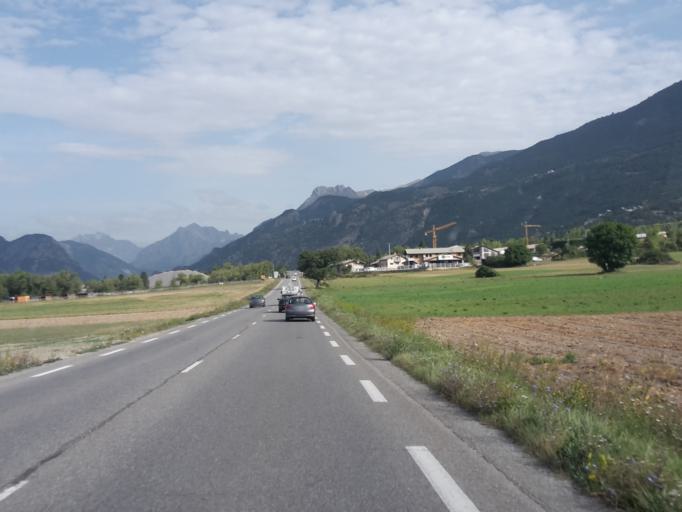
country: FR
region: Provence-Alpes-Cote d'Azur
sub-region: Departement des Hautes-Alpes
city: Guillestre
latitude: 44.6798
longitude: 6.6157
